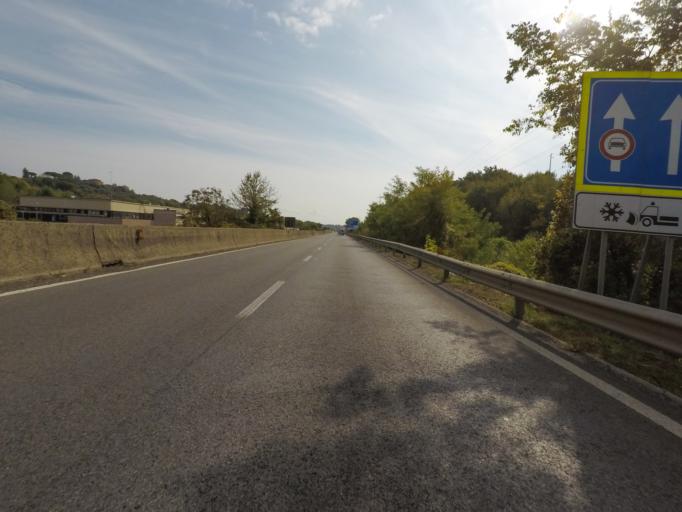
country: IT
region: Tuscany
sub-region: Provincia di Siena
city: Siena
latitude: 43.3049
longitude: 11.3181
